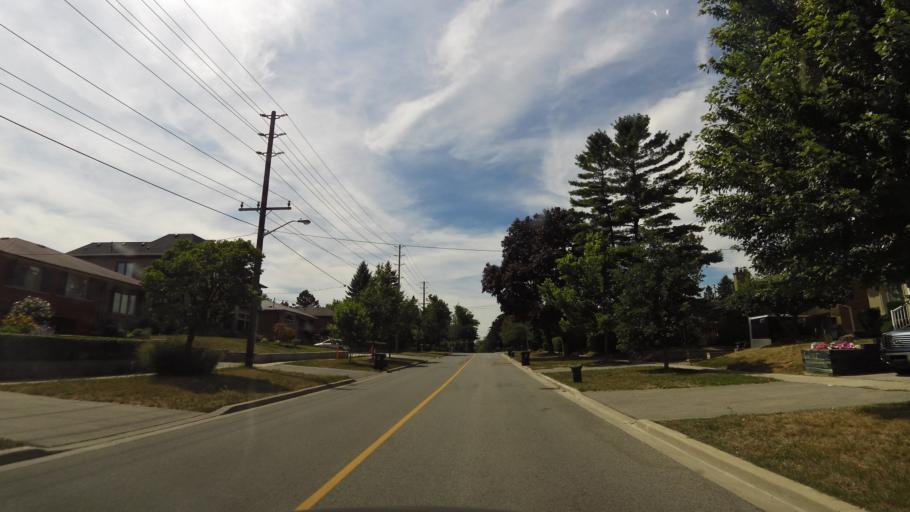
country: CA
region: Ontario
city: Etobicoke
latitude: 43.6355
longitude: -79.4967
